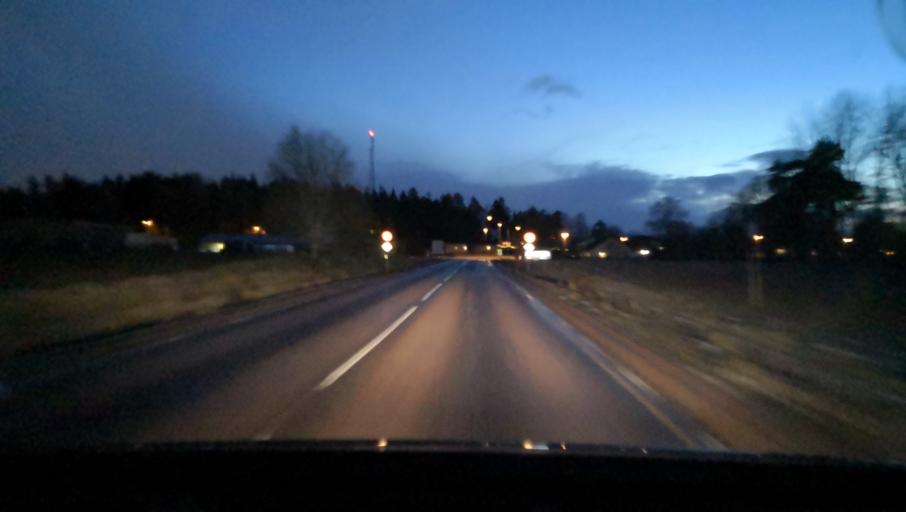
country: SE
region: Vaestmanland
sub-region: Vasteras
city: Skultuna
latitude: 59.7265
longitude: 16.4323
